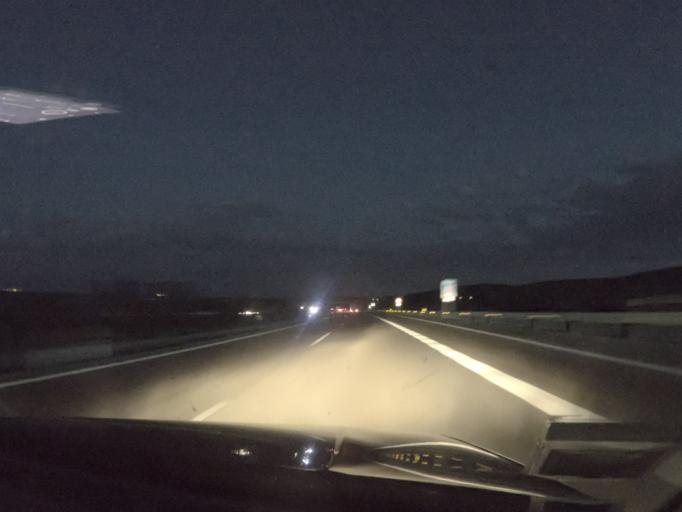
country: ES
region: Castille and Leon
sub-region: Provincia de Leon
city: Brazuelo
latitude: 42.5341
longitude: -6.1509
